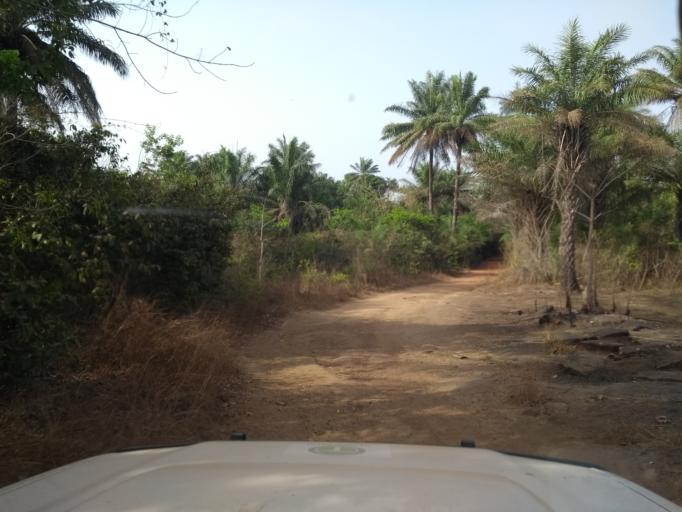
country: GN
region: Kindia
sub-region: Prefecture de Dubreka
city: Dubreka
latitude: 9.8183
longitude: -13.5567
